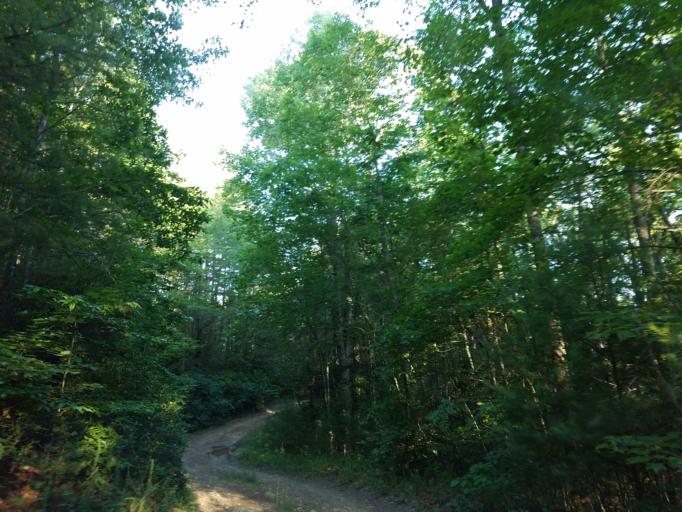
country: US
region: Georgia
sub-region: Fannin County
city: Blue Ridge
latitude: 34.8156
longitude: -84.1494
